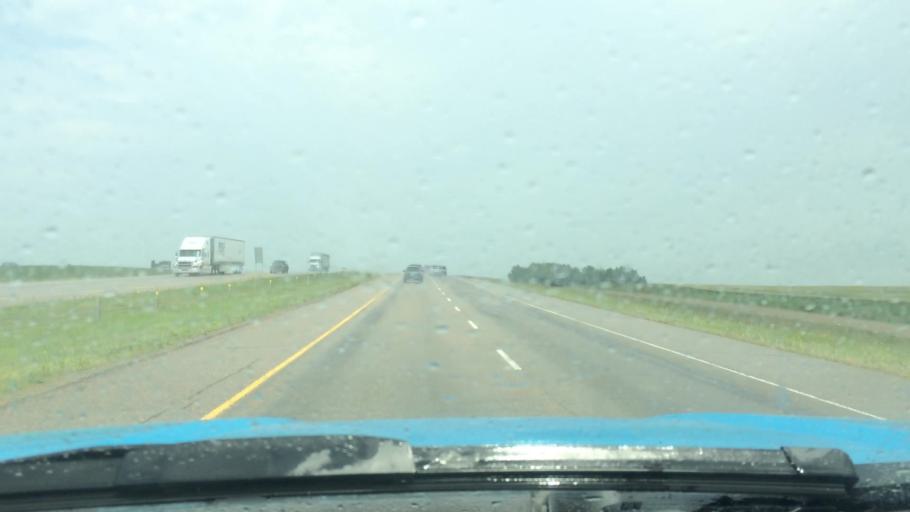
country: CA
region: Alberta
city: Carstairs
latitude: 51.5789
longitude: -114.0251
